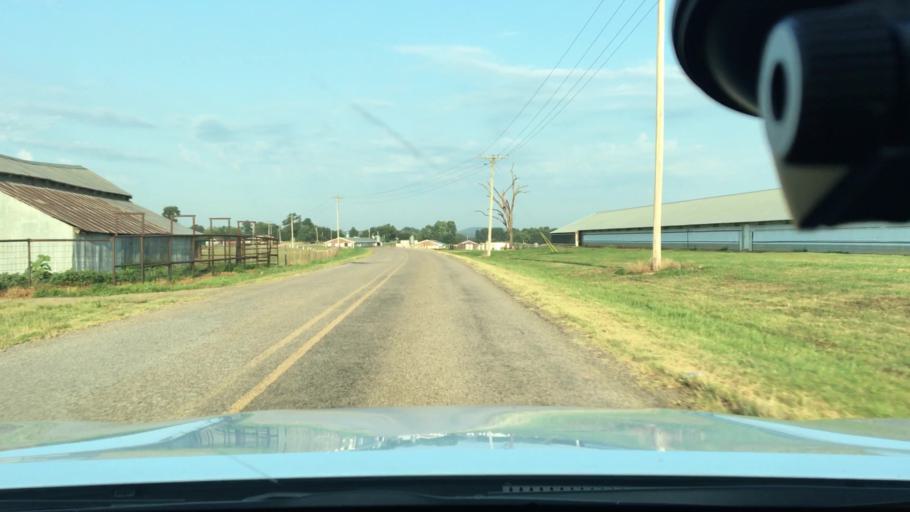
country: US
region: Arkansas
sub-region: Johnson County
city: Coal Hill
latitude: 35.3731
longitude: -93.5723
